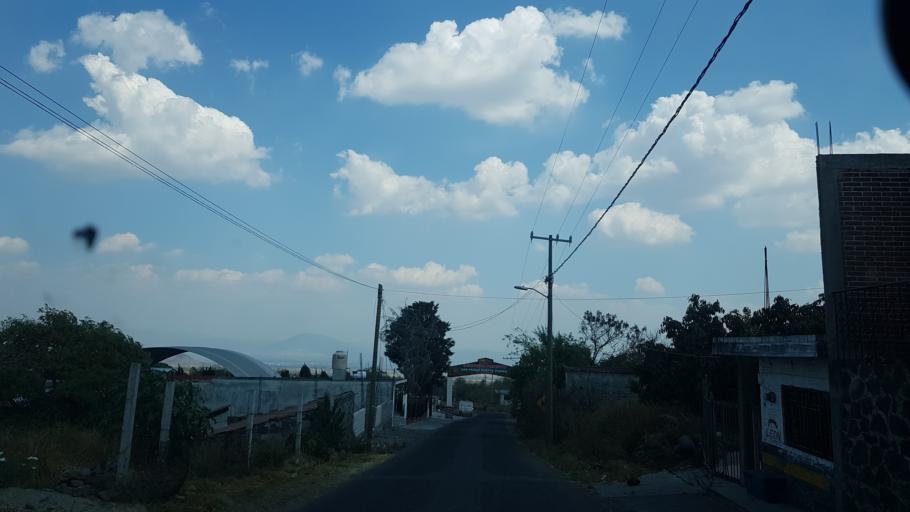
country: MX
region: Puebla
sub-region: Atlixco
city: San Pedro Benito Juarez
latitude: 18.9498
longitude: -98.5414
